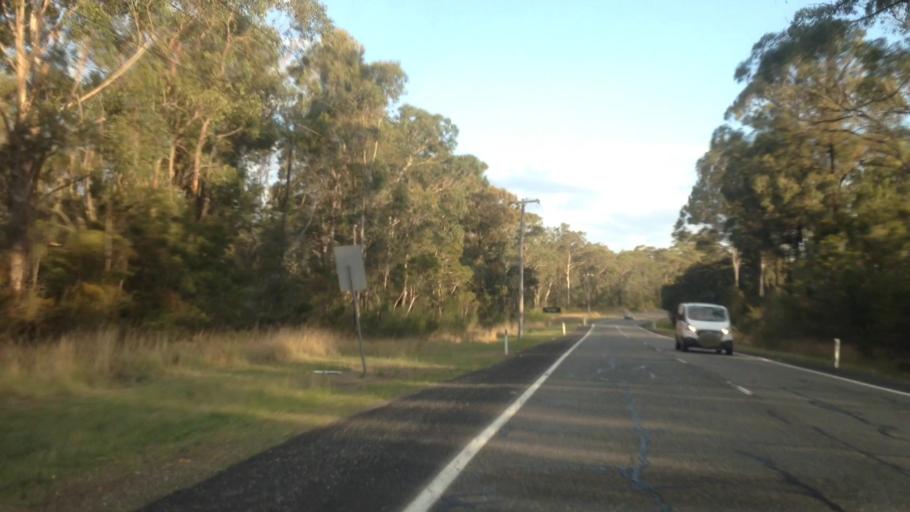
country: AU
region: New South Wales
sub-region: Cessnock
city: Kurri Kurri
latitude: -32.8372
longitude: 151.4825
